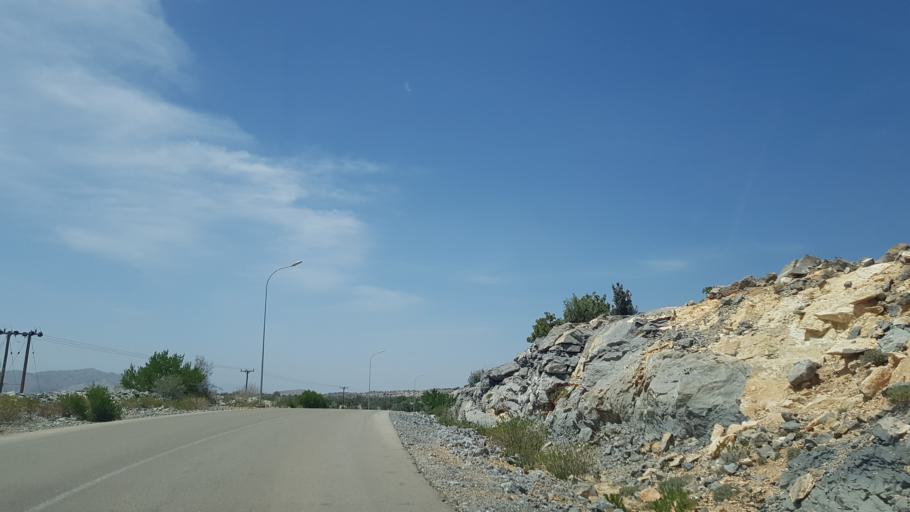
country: OM
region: Al Batinah
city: Bayt al `Awabi
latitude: 23.1252
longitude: 57.6000
